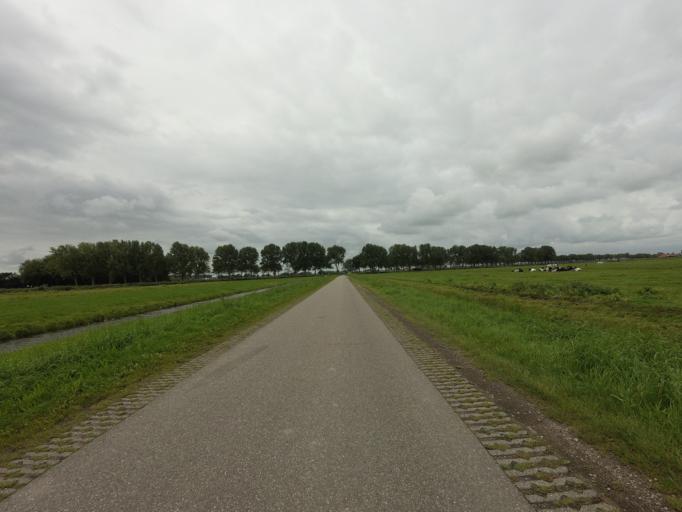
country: NL
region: North Holland
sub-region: Gemeente Edam-Volendam
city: Edam
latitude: 52.5435
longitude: 5.0283
